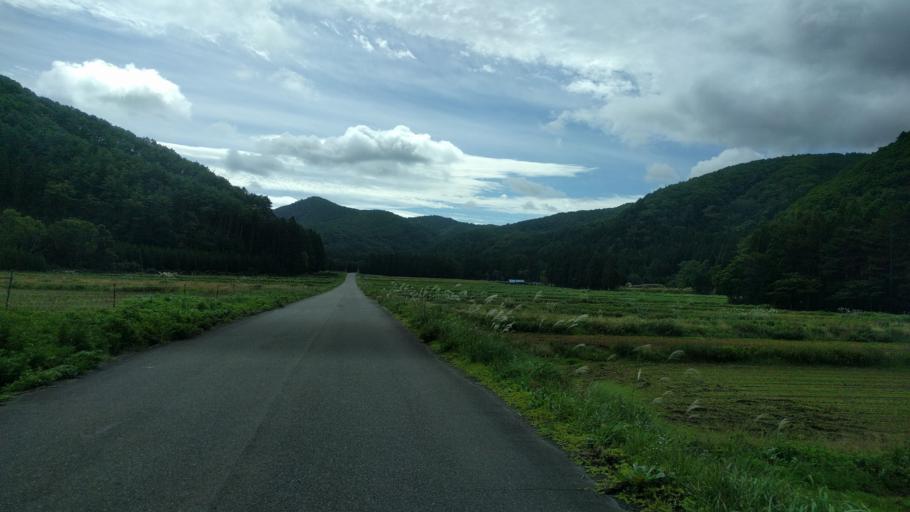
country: JP
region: Fukushima
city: Inawashiro
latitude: 37.3852
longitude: 140.1504
